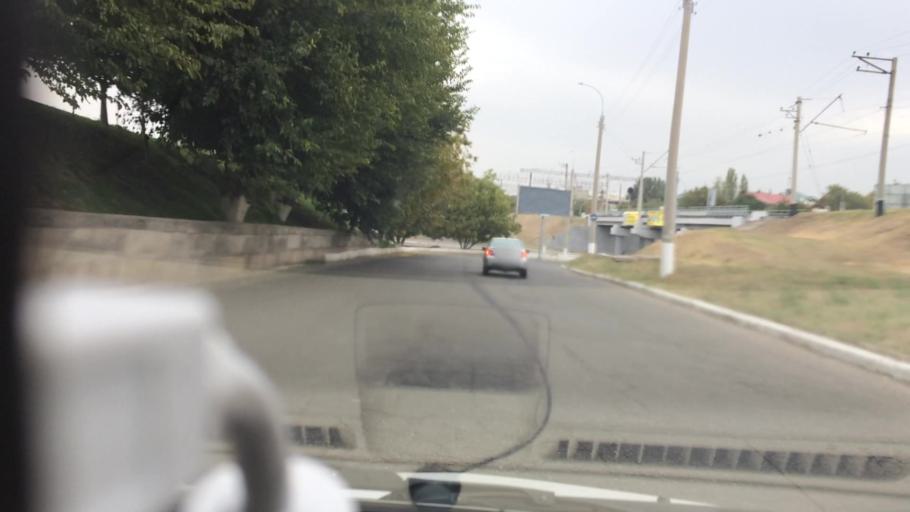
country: UZ
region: Toshkent
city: Salor
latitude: 41.3177
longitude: 69.3114
